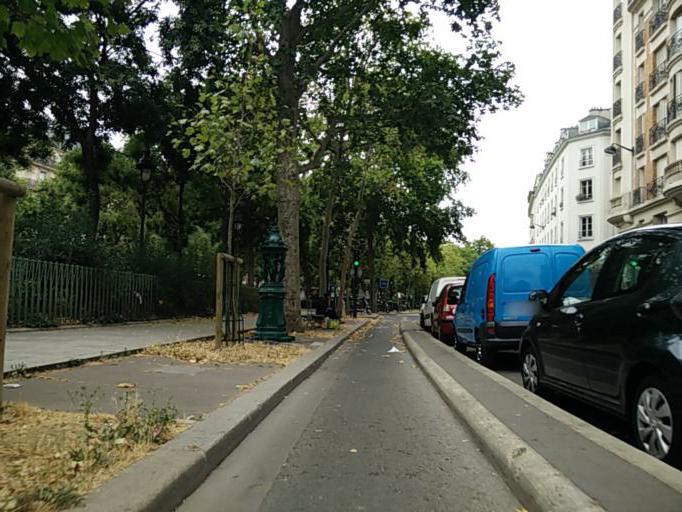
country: FR
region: Ile-de-France
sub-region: Paris
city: Paris
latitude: 48.8624
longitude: 2.3720
